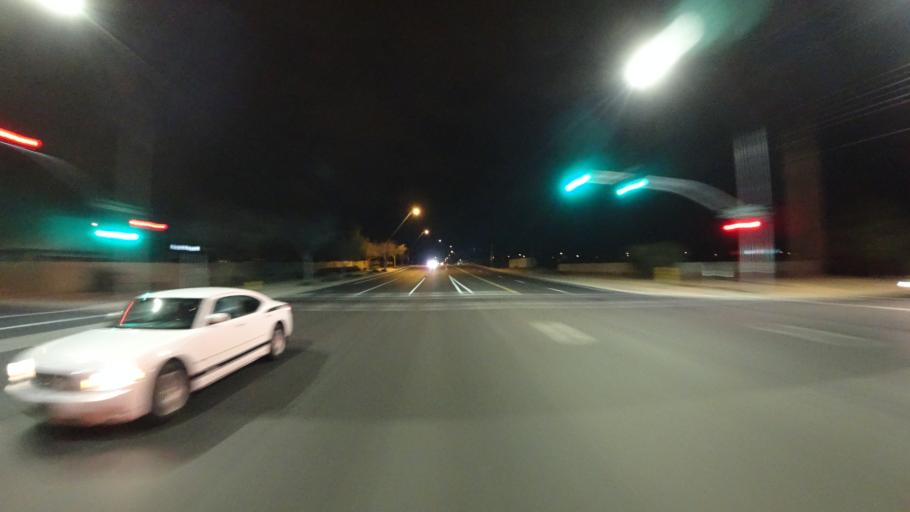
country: US
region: Arizona
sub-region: Pinal County
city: Apache Junction
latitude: 33.3993
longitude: -111.5981
